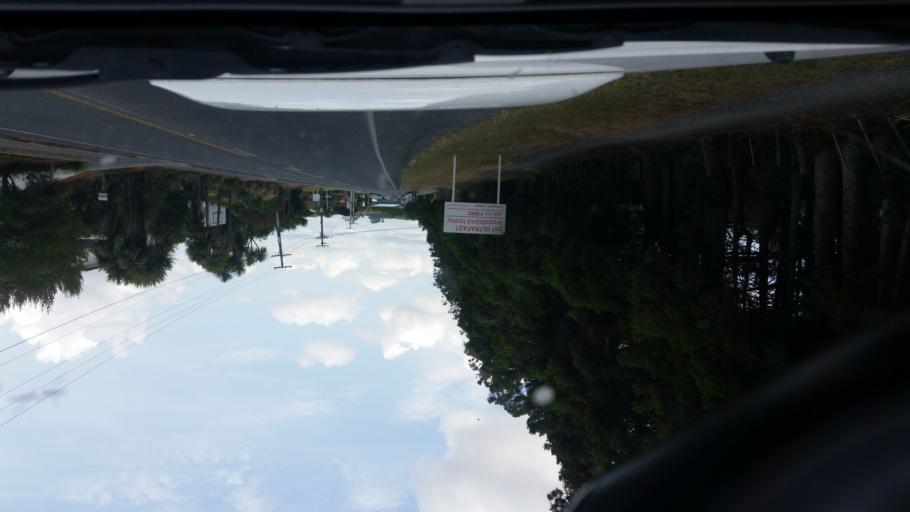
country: NZ
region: Auckland
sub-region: Auckland
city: Wellsford
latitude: -36.1229
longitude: 174.5724
